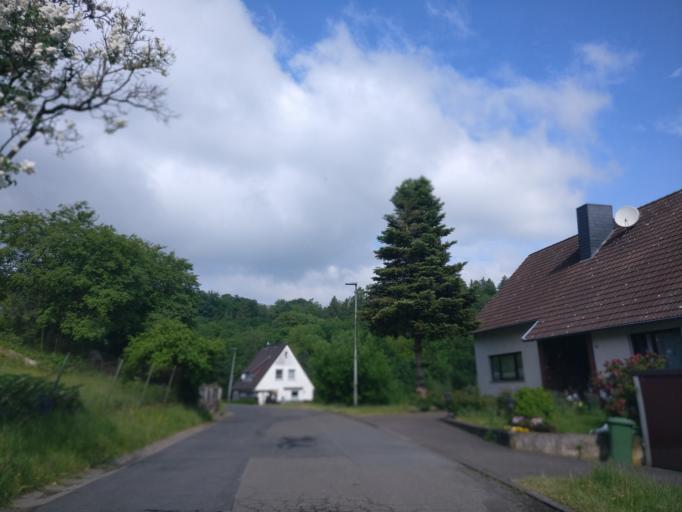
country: DE
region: Lower Saxony
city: Scheden
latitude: 51.3983
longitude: 9.7078
